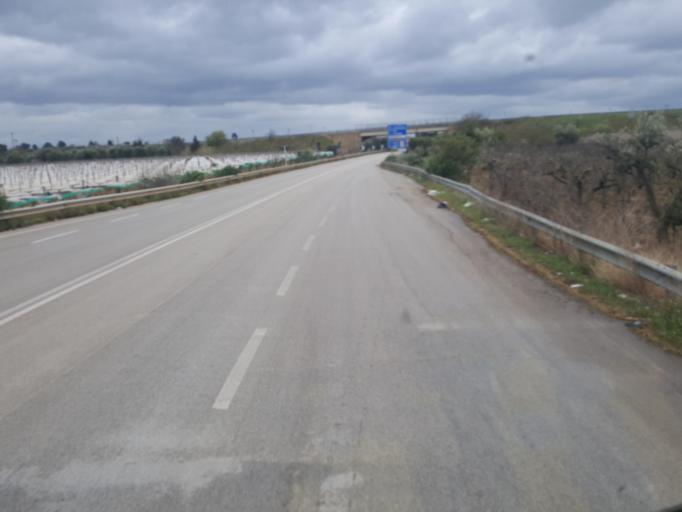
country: IT
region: Apulia
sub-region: Provincia di Bari
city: Conversano
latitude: 40.9824
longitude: 17.0858
